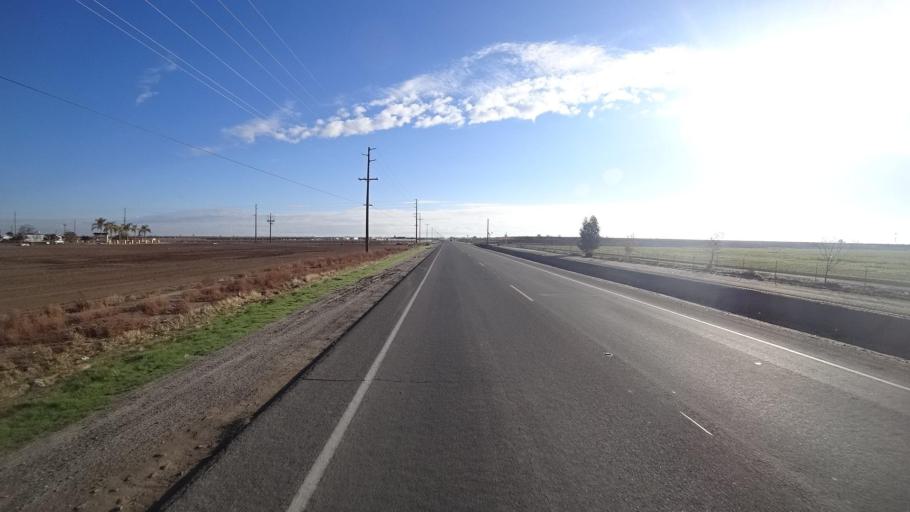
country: US
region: California
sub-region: Kern County
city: Delano
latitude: 35.7759
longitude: -119.2957
